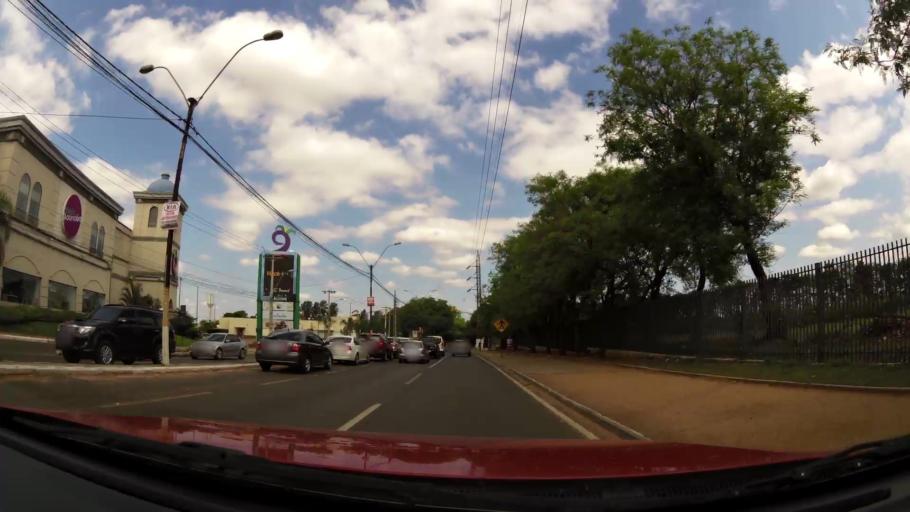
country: PY
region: Central
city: Fernando de la Mora
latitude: -25.3240
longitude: -57.5212
